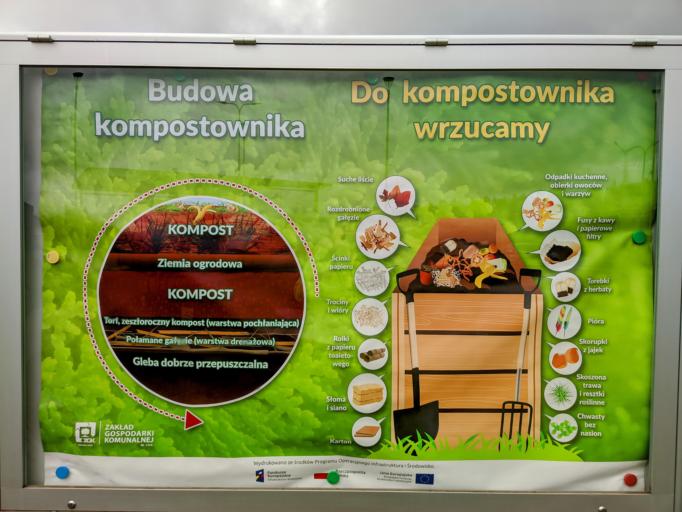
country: PL
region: Lubusz
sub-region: Zielona Gora
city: Zielona Gora
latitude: 51.9180
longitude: 15.5462
